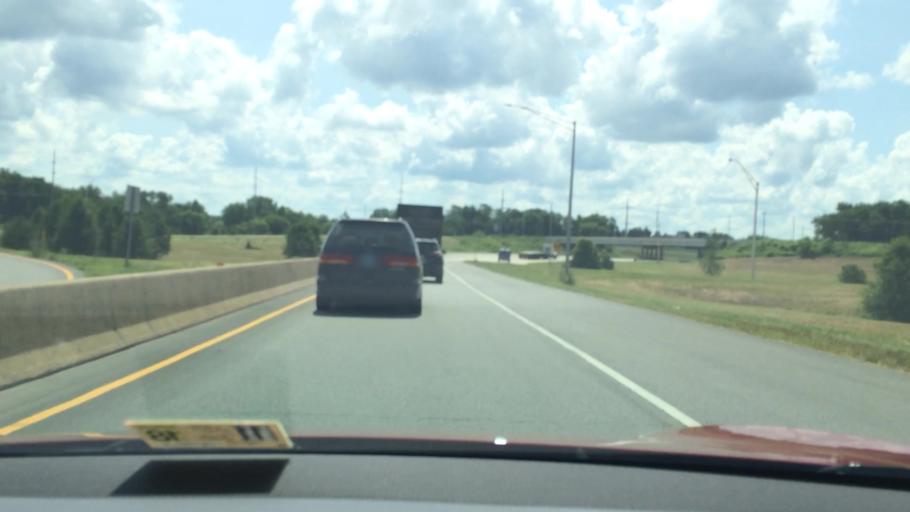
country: US
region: Indiana
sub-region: Saint Joseph County
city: South Bend
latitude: 41.7249
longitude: -86.3411
